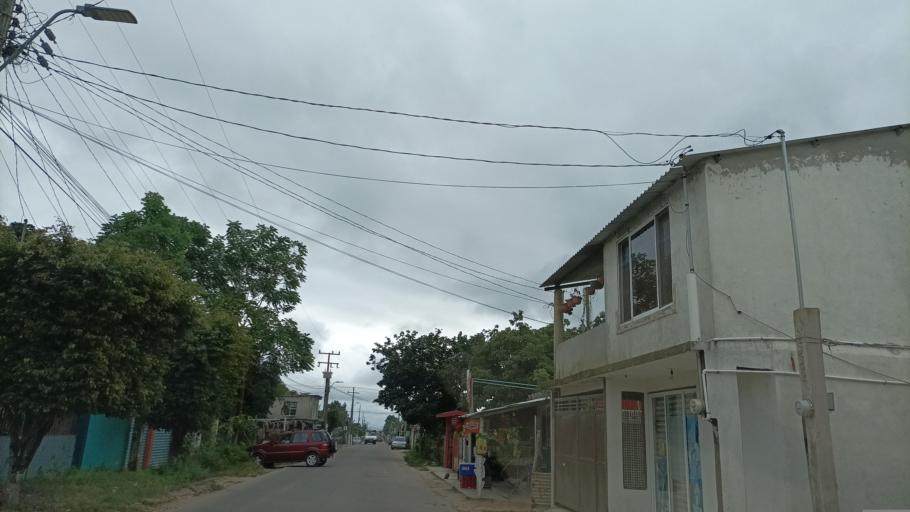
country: MX
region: Veracruz
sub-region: Cosoleacaque
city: Residencial las Olas
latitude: 18.0699
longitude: -94.5883
